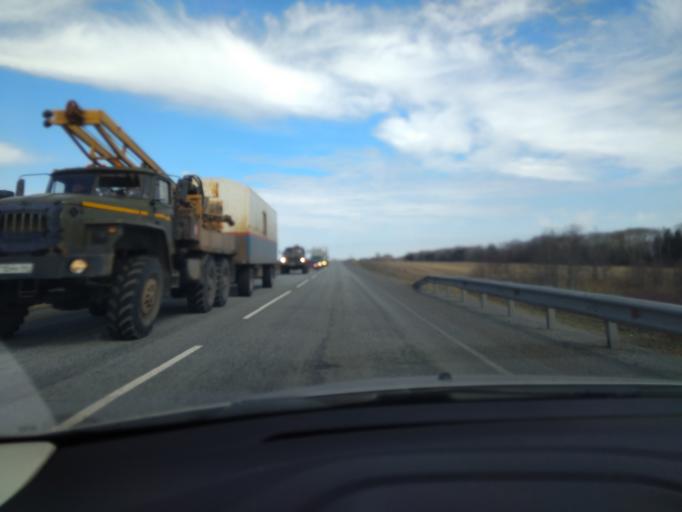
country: RU
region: Sverdlovsk
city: Pyshma
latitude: 57.0089
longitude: 63.3449
